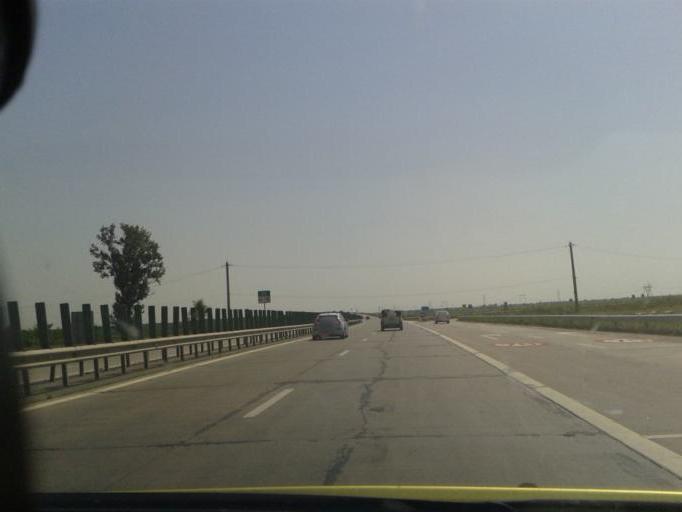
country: RO
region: Ilfov
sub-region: Comuna Cernica
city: Caldararu
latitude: 44.4084
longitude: 26.2721
